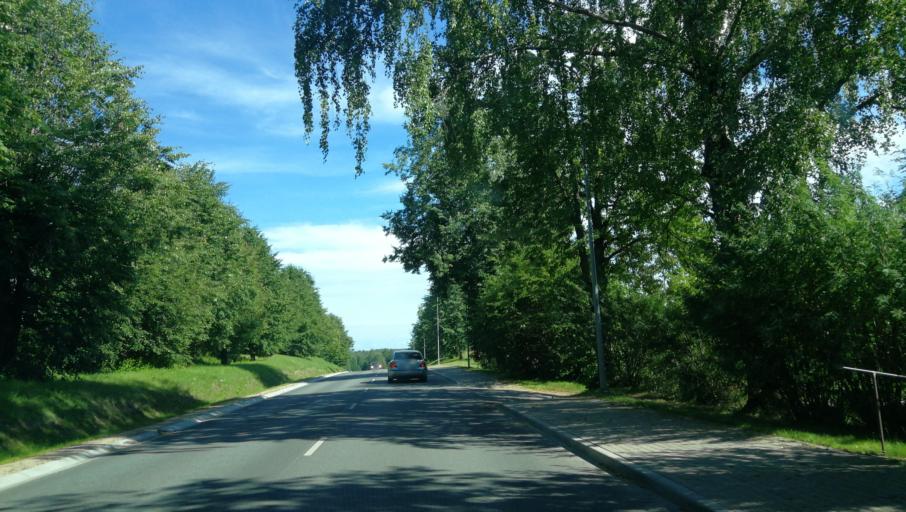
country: LV
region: Cesvaine
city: Cesvaine
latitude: 56.9659
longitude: 26.3192
